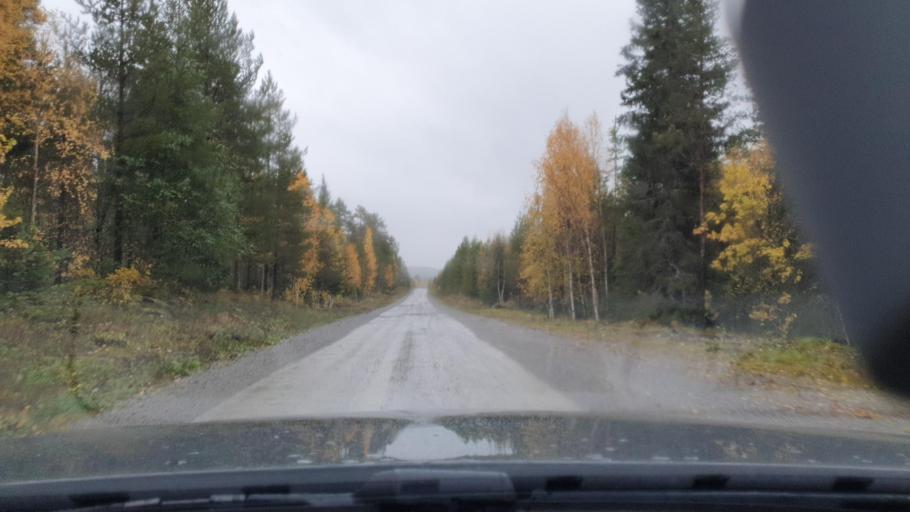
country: SE
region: Jaemtland
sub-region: Stroemsunds Kommun
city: Stroemsund
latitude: 63.5425
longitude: 15.5718
